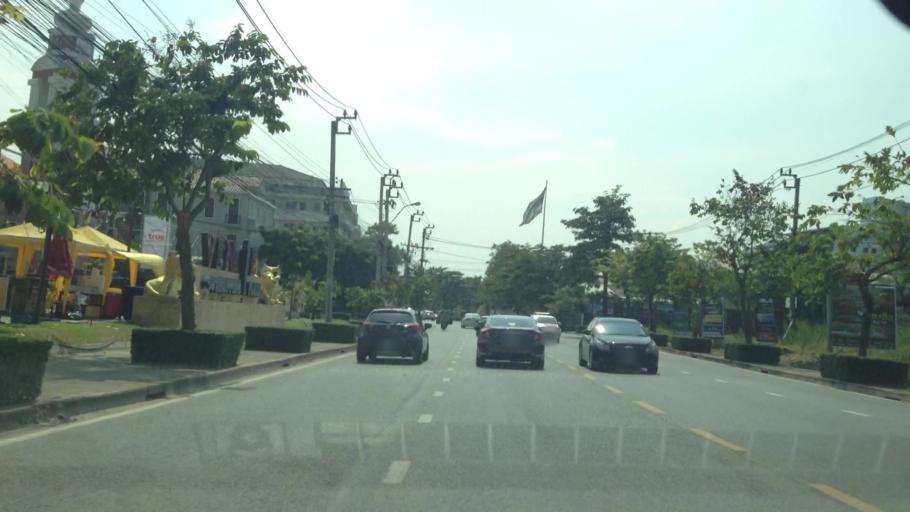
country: TH
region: Bangkok
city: Bang Khen
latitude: 13.8797
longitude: 100.6432
